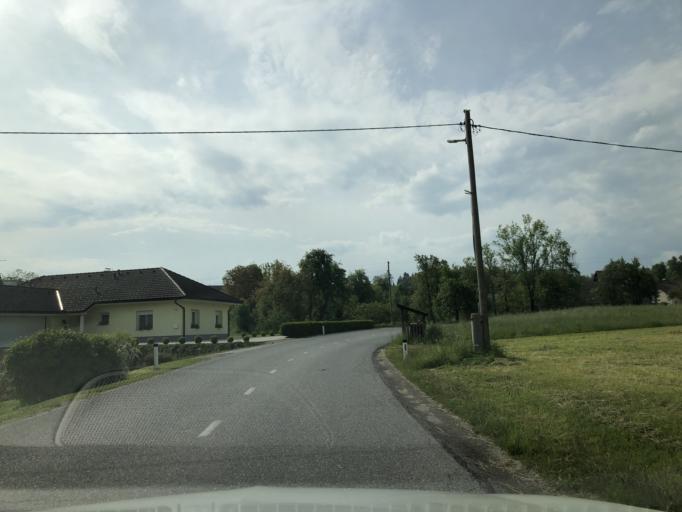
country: SI
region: Velike Lasce
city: Velike Lasce
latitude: 45.8105
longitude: 14.6260
